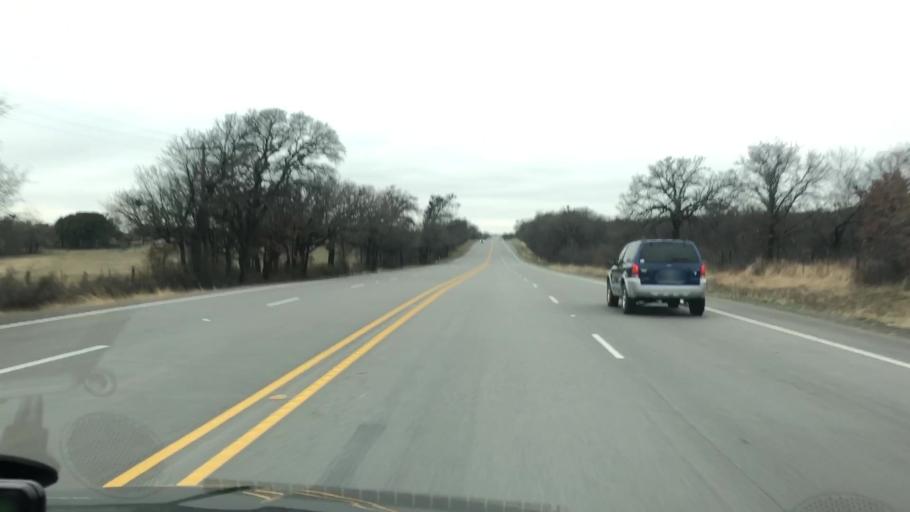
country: US
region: Texas
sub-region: Hamilton County
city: Hico
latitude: 32.0104
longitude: -98.0611
